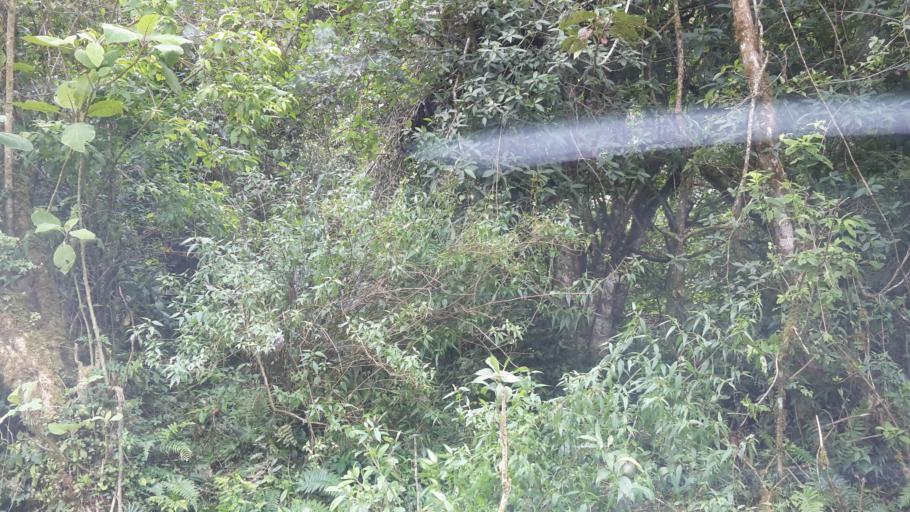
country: BO
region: Cochabamba
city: Totora
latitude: -17.4962
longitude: -65.2729
